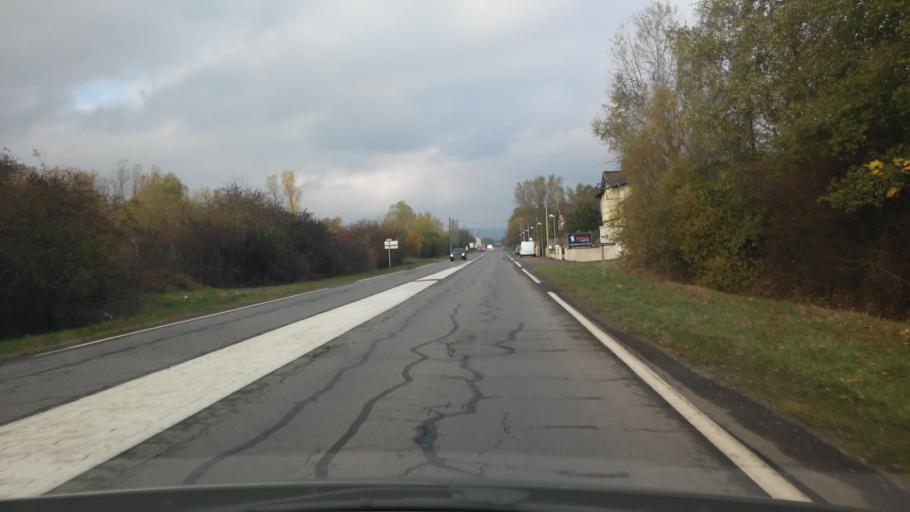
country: FR
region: Lorraine
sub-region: Departement de la Moselle
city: Uckange
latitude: 49.3148
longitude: 6.1574
